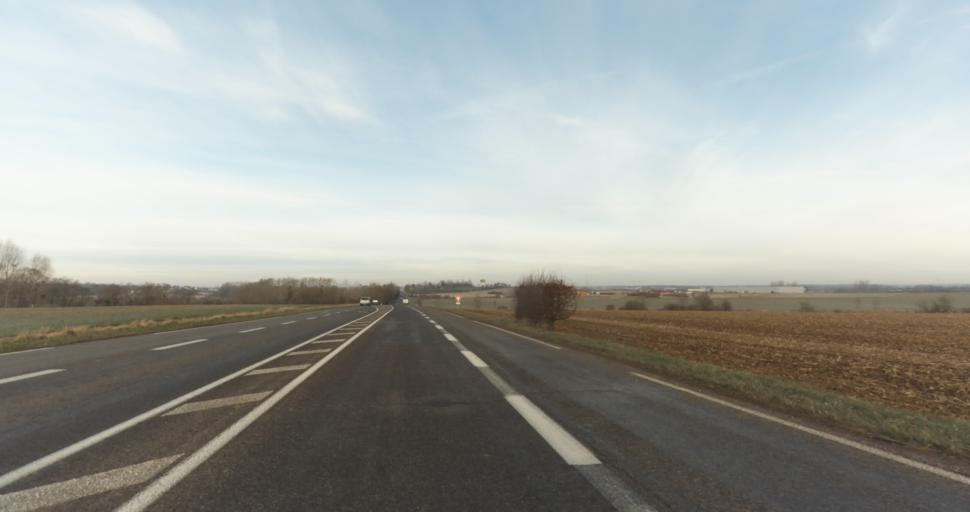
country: FR
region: Lorraine
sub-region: Departement de Meurthe-et-Moselle
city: Giraumont
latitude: 49.1497
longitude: 5.9107
